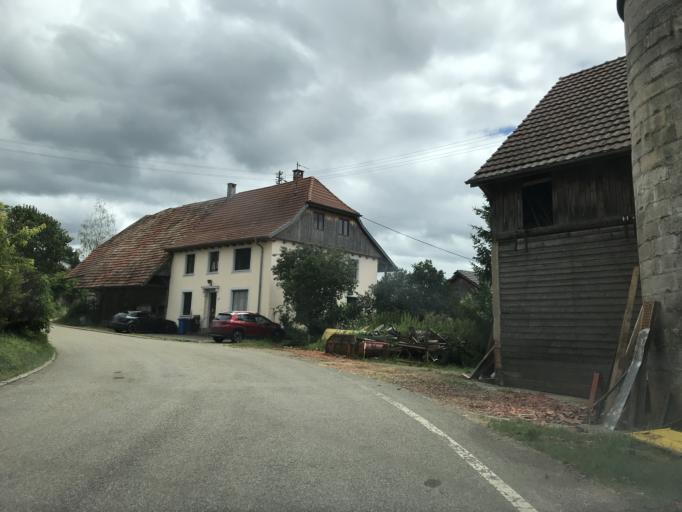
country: DE
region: Baden-Wuerttemberg
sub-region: Freiburg Region
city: Hasel
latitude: 47.6648
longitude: 7.8687
